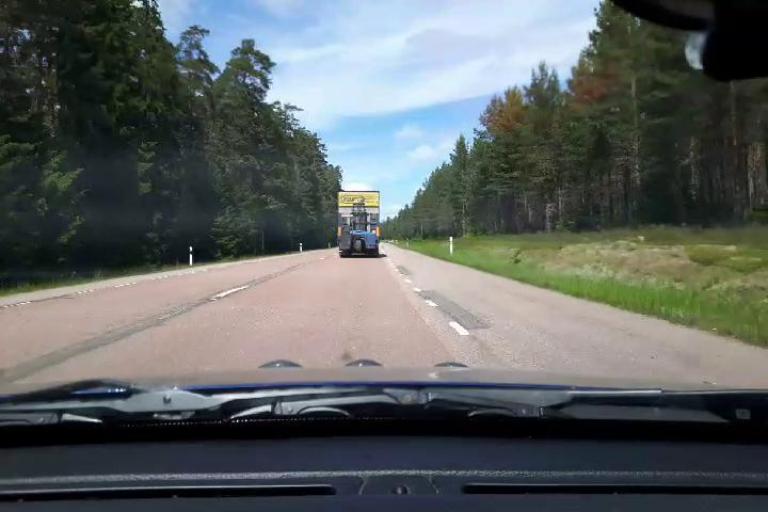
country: SE
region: Uppsala
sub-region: Osthammars Kommun
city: Bjorklinge
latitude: 60.1257
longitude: 17.5092
